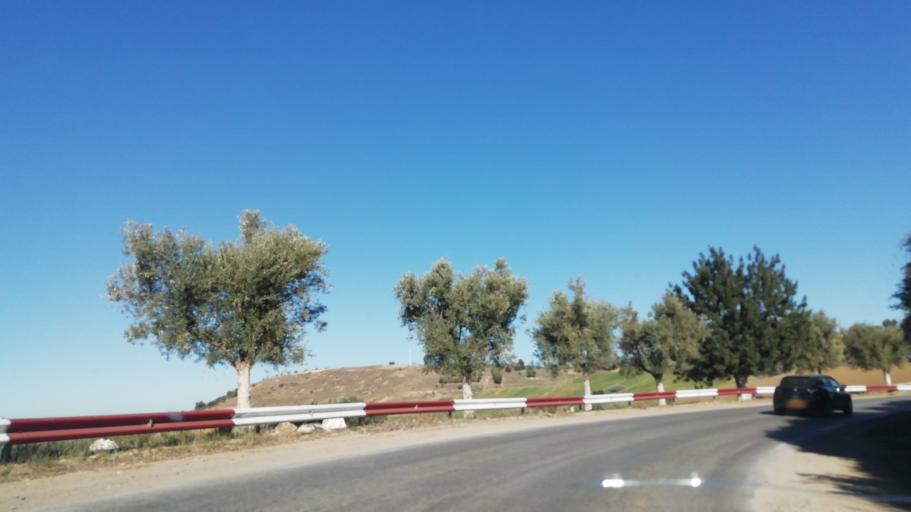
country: DZ
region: Tlemcen
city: Beni Mester
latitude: 34.8300
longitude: -1.5066
